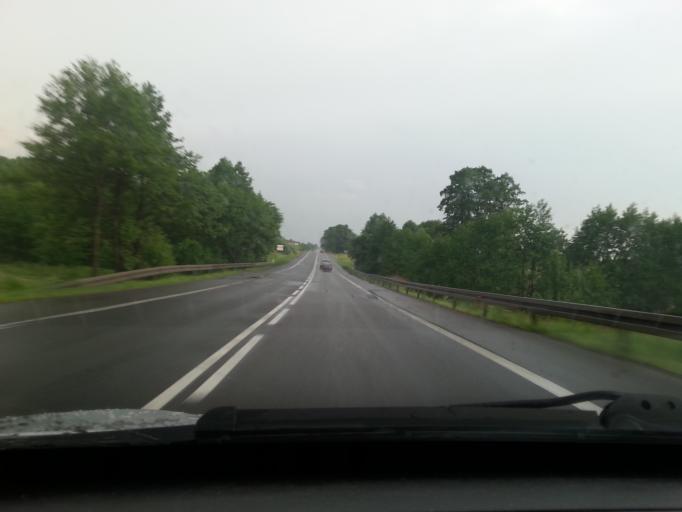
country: PL
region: Lodz Voivodeship
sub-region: Powiat zgierski
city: Strykow
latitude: 51.8638
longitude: 19.5675
